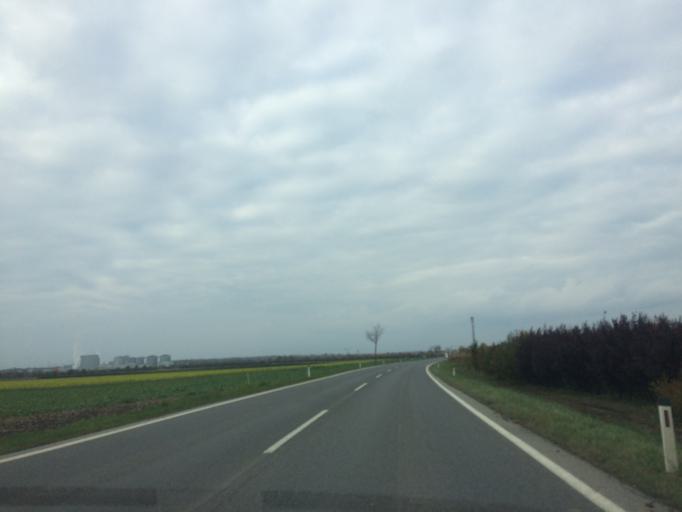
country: AT
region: Lower Austria
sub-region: Politischer Bezirk Tulln
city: Tulln
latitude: 48.3085
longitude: 16.0570
